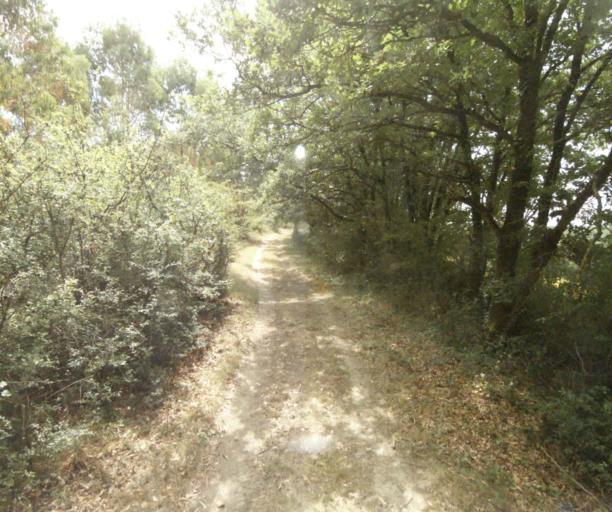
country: FR
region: Midi-Pyrenees
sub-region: Departement de la Haute-Garonne
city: Saint-Felix-Lauragais
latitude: 43.4228
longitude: 1.9320
